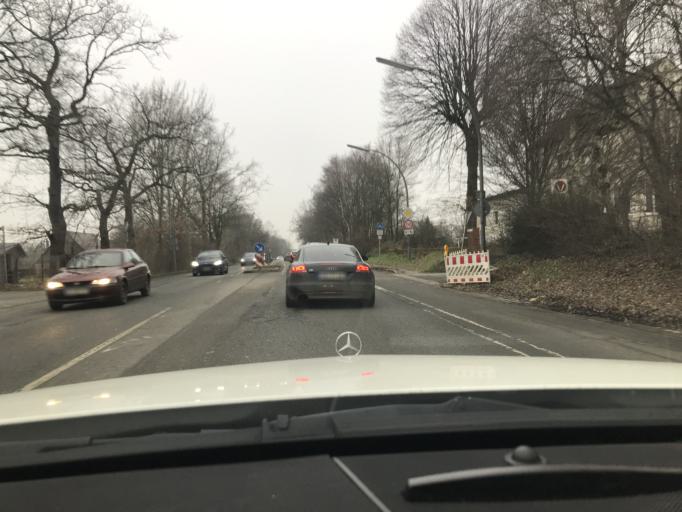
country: DE
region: North Rhine-Westphalia
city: Waltrop
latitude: 51.6007
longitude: 7.3931
